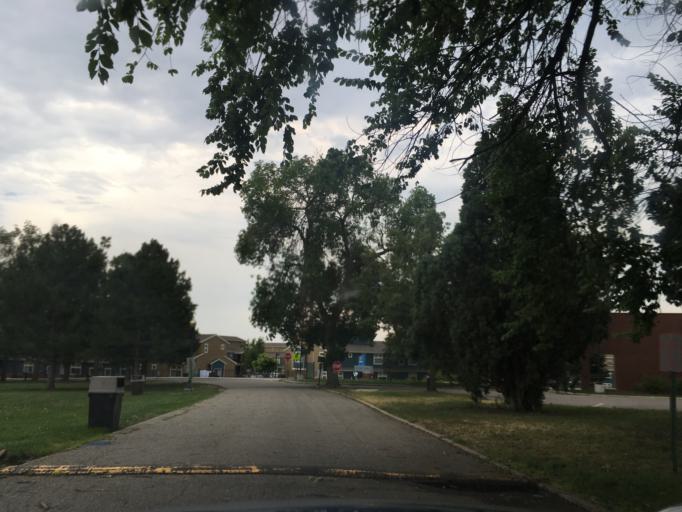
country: US
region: Colorado
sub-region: Arapahoe County
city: Sheridan
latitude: 39.6611
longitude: -105.0266
